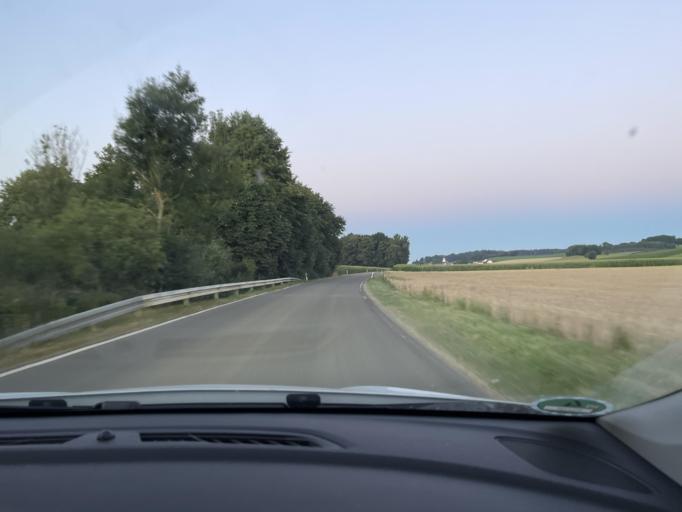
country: DE
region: Bavaria
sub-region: Swabia
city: Aichach
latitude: 48.4394
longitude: 11.1005
